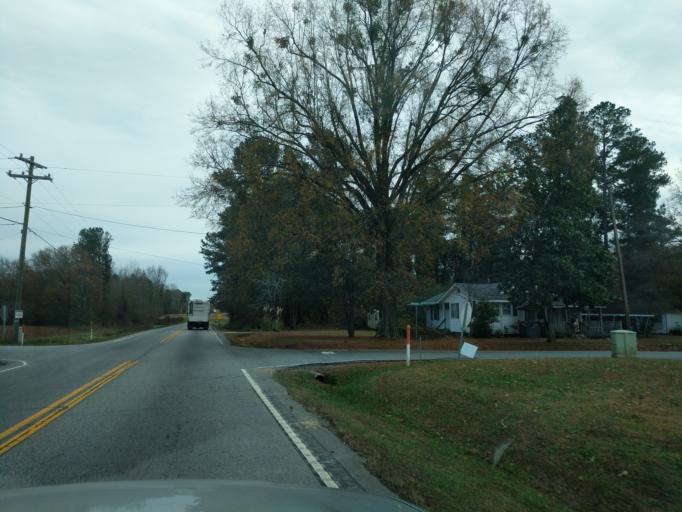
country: US
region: South Carolina
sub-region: Anderson County
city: Piedmont
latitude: 34.6729
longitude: -82.5317
